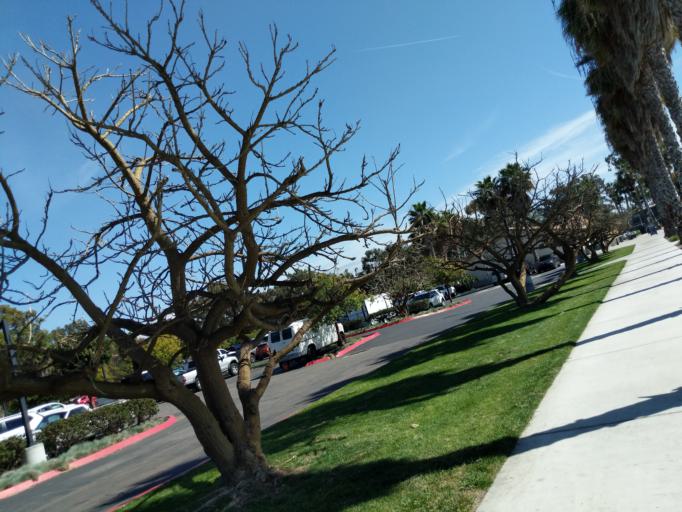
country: US
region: California
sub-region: San Diego County
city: La Jolla
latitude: 32.7635
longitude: -117.2364
